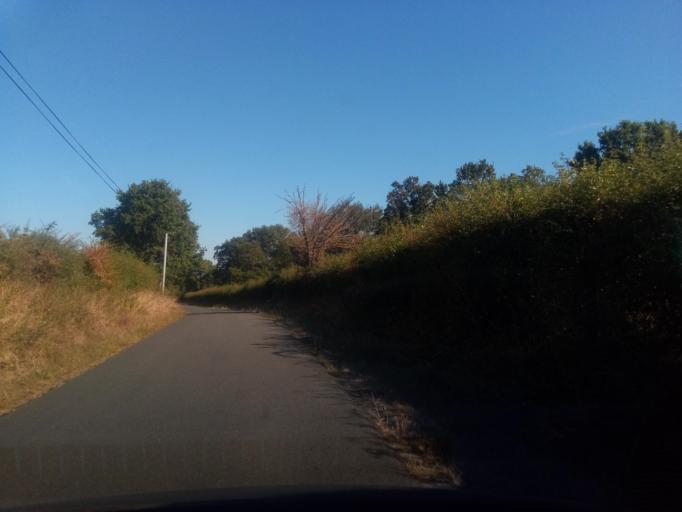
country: FR
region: Poitou-Charentes
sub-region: Departement de la Vienne
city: Montmorillon
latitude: 46.4251
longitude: 0.8361
